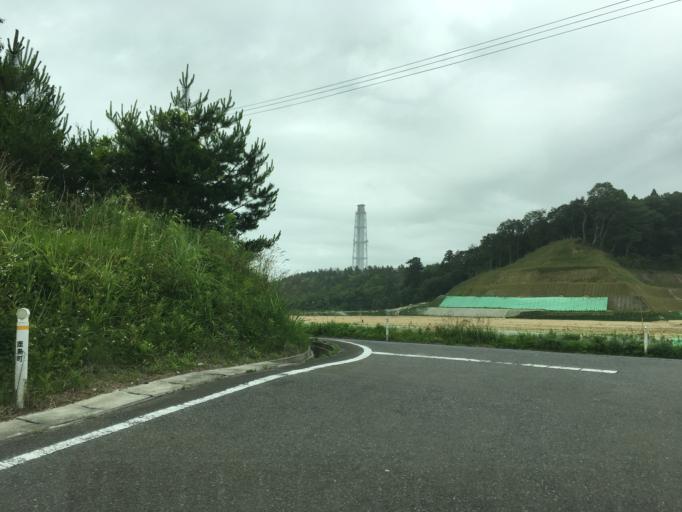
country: JP
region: Fukushima
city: Namie
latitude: 37.6750
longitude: 141.0114
